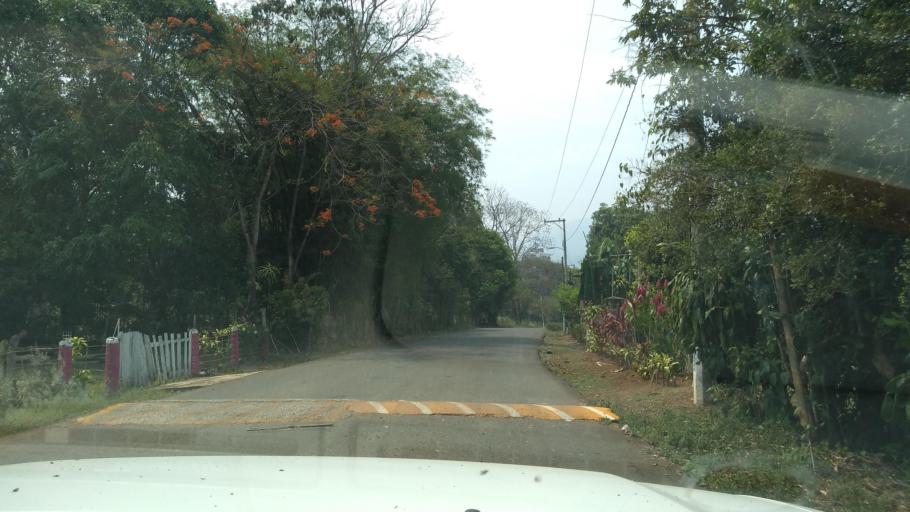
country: MX
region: Veracruz
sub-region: Tezonapa
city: Laguna Chica (Pueblo Nuevo)
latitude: 18.5402
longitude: -96.7698
